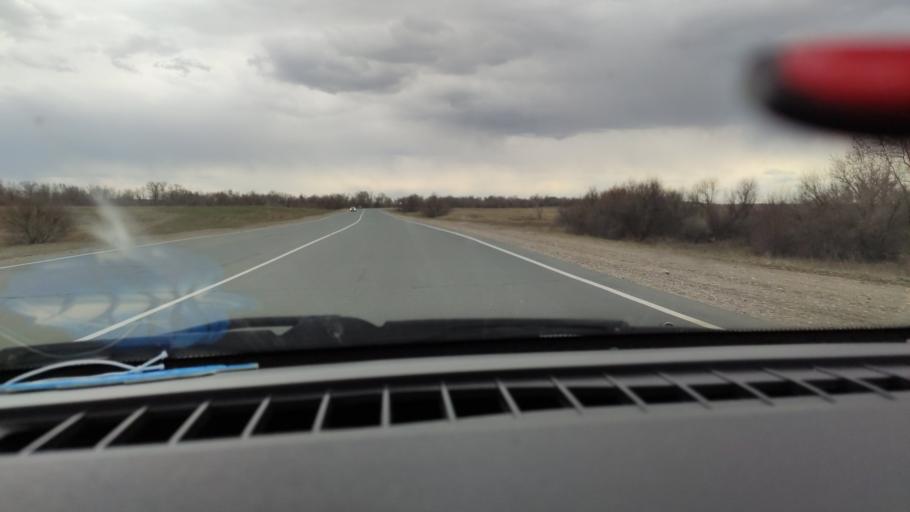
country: RU
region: Saratov
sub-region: Saratovskiy Rayon
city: Saratov
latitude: 51.7161
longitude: 46.0254
